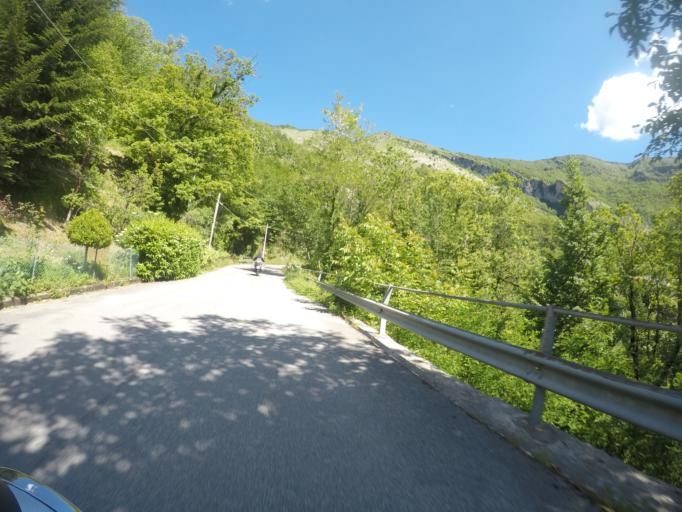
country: IT
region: Tuscany
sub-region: Provincia di Lucca
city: Fontana delle Monache
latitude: 44.0665
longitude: 10.3078
